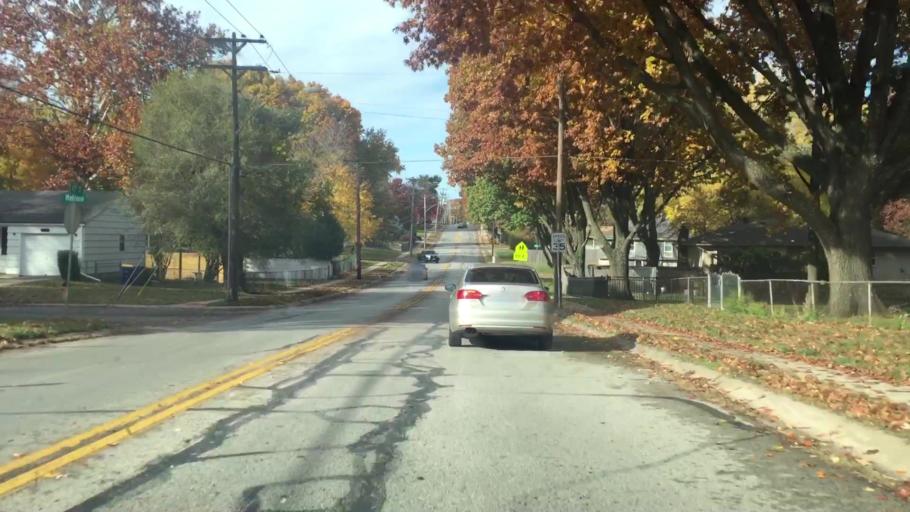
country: US
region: Kansas
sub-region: Johnson County
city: Merriam
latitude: 39.0076
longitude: -94.7079
